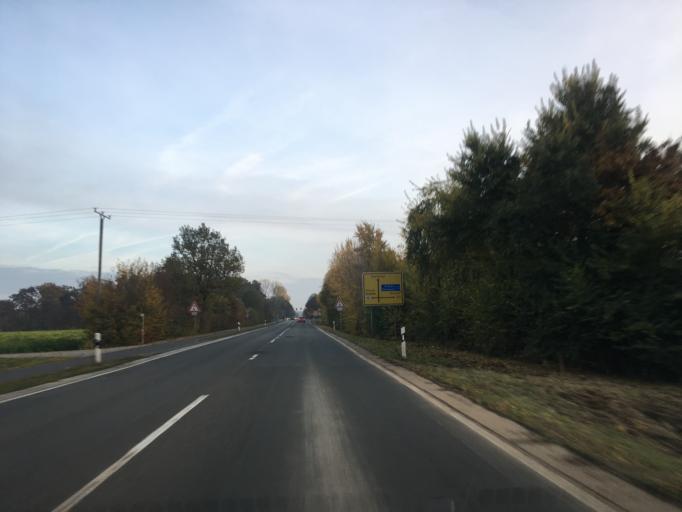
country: DE
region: North Rhine-Westphalia
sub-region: Regierungsbezirk Munster
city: Altenberge
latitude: 52.0749
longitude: 7.4345
